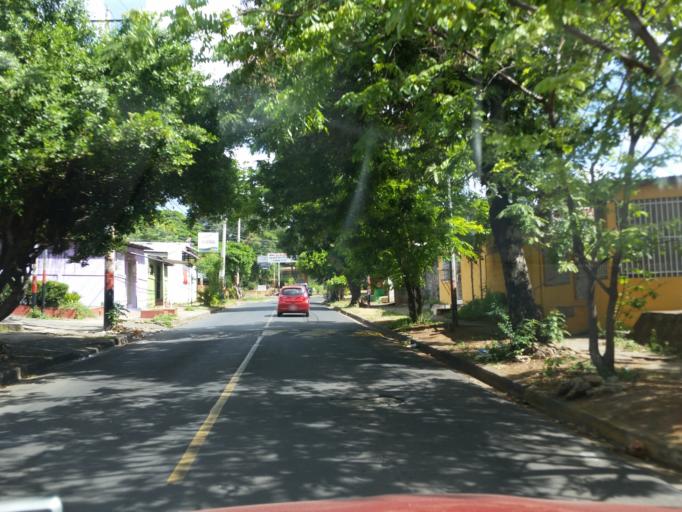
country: NI
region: Managua
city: Managua
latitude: 12.1122
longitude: -86.2484
